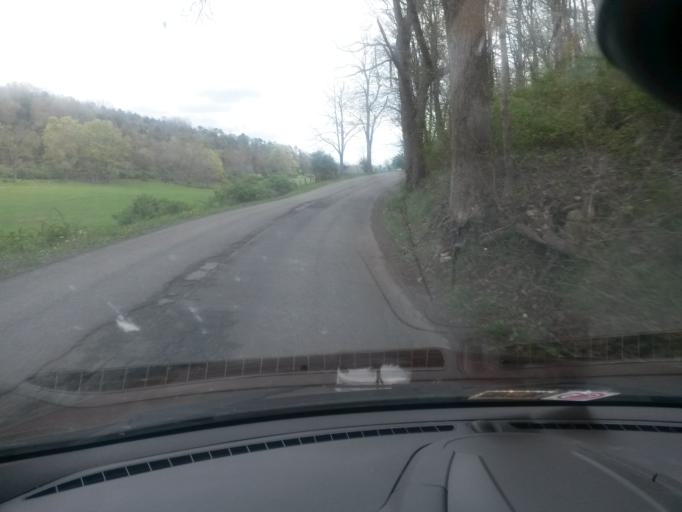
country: US
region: West Virginia
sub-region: Greenbrier County
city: Lewisburg
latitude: 37.8926
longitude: -80.4325
